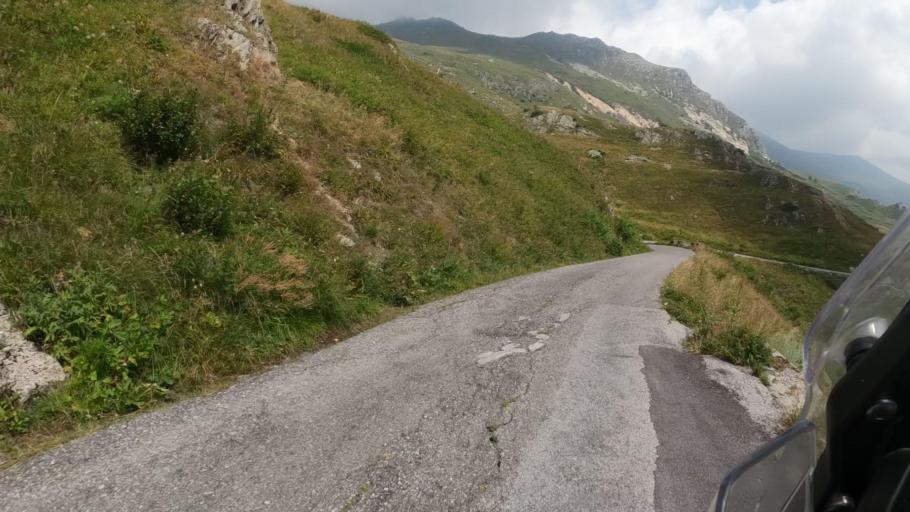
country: IT
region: Piedmont
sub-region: Provincia di Cuneo
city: Campomolino
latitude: 44.3931
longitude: 7.1506
